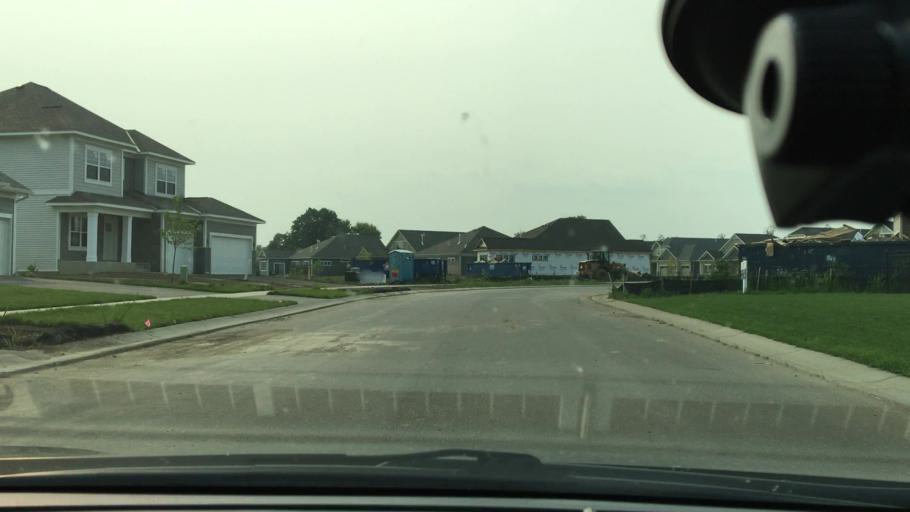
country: US
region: Minnesota
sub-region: Anoka County
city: Ramsey
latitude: 45.2150
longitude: -93.4649
